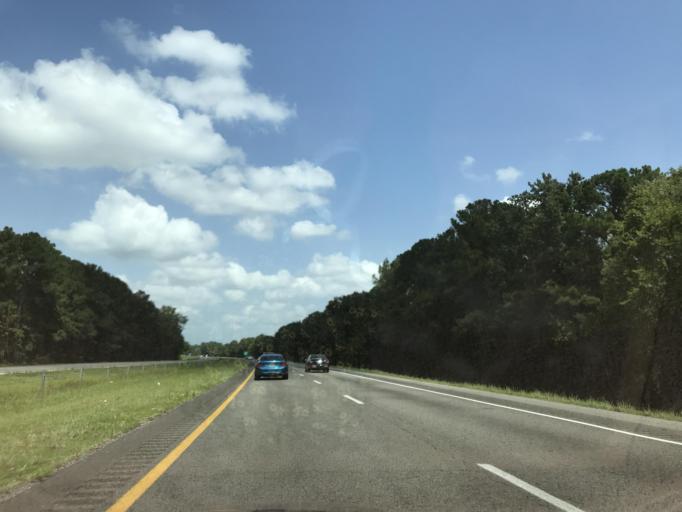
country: US
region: North Carolina
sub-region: Pender County
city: Rocky Point
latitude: 34.4191
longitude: -77.8691
